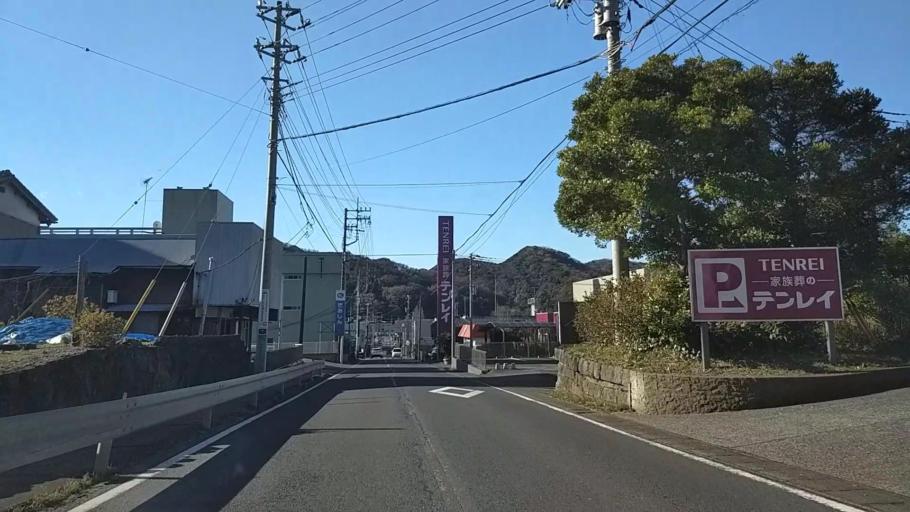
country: JP
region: Chiba
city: Futtsu
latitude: 35.2177
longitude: 139.8720
